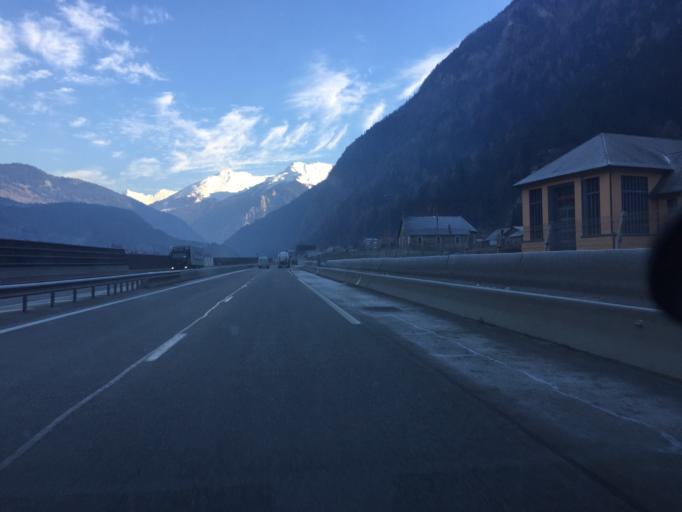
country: FR
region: Rhone-Alpes
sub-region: Departement de la Savoie
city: Modane
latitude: 45.2031
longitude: 6.5852
